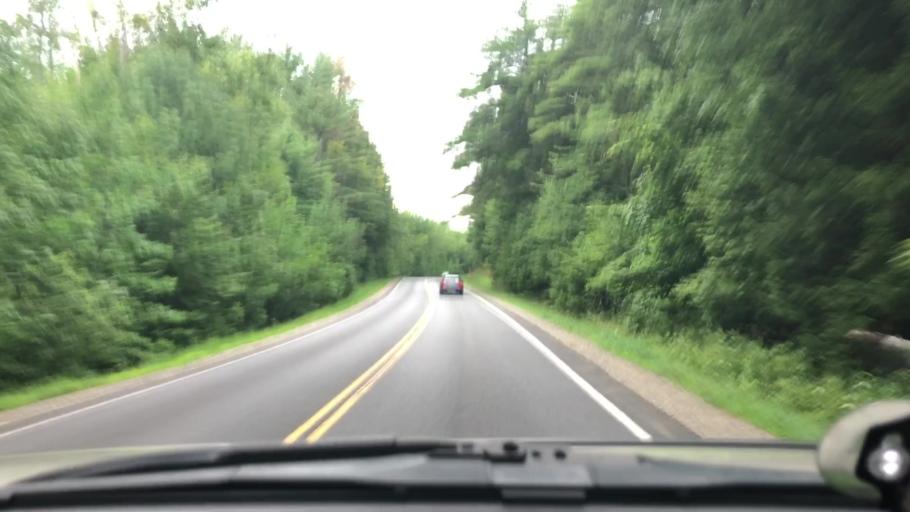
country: US
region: New York
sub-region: Saratoga County
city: Corinth
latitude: 43.2044
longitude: -73.7696
